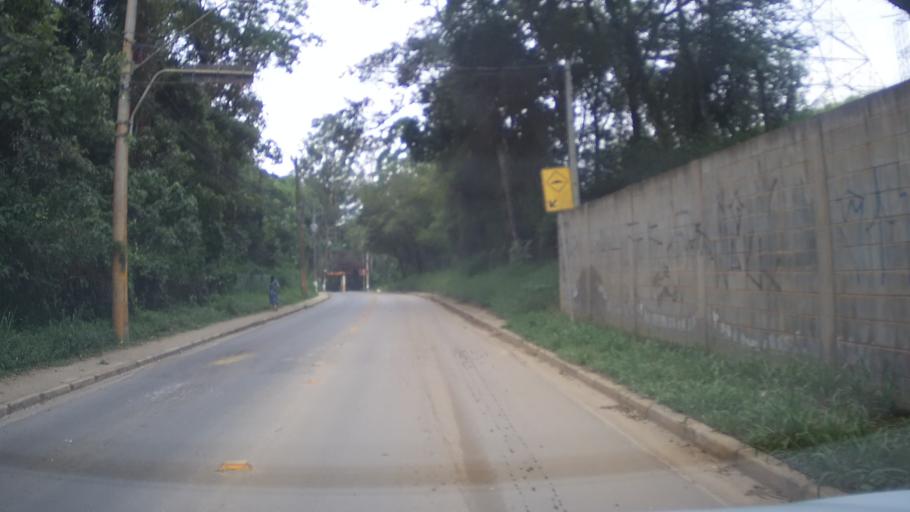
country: BR
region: Sao Paulo
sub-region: Aruja
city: Aruja
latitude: -23.3726
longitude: -46.4008
